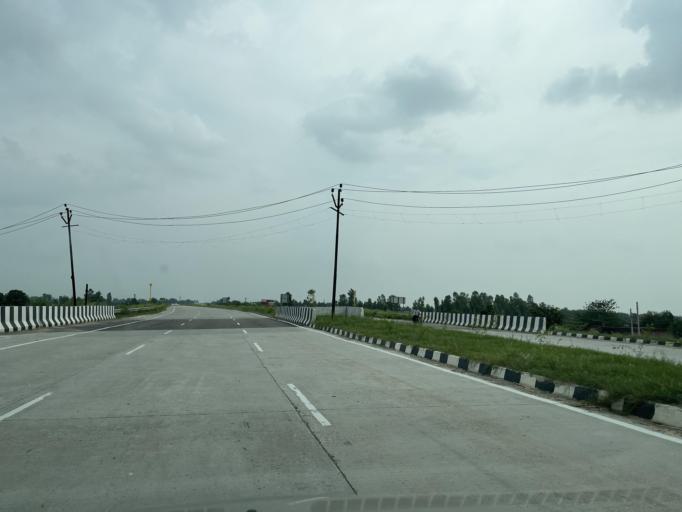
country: IN
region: Uttarakhand
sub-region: Udham Singh Nagar
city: Kashipur
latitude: 29.2022
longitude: 78.9324
